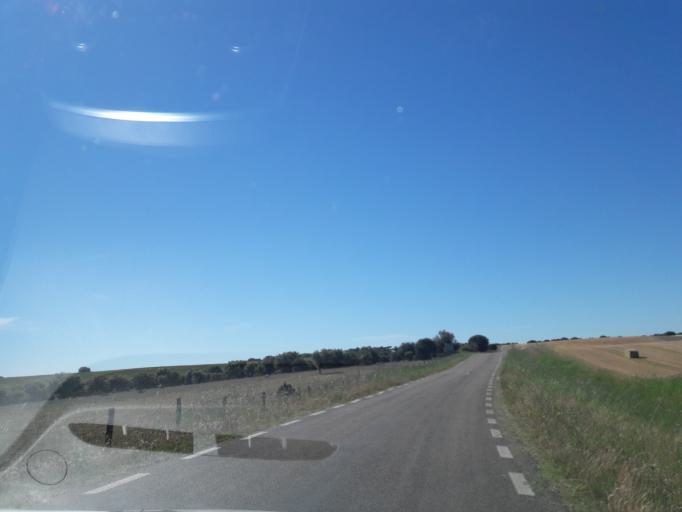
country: ES
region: Castille and Leon
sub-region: Provincia de Salamanca
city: Zarapicos
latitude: 41.0333
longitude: -5.8390
